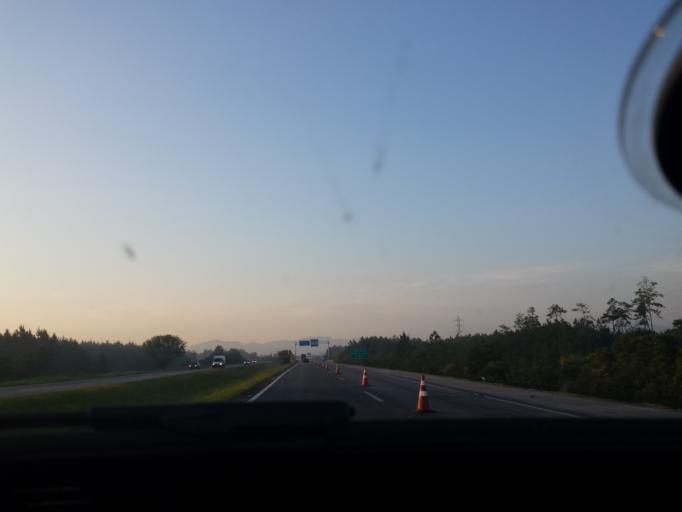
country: BR
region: Santa Catarina
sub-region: Florianopolis
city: Pantano do Sul
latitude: -27.8714
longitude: -48.6467
